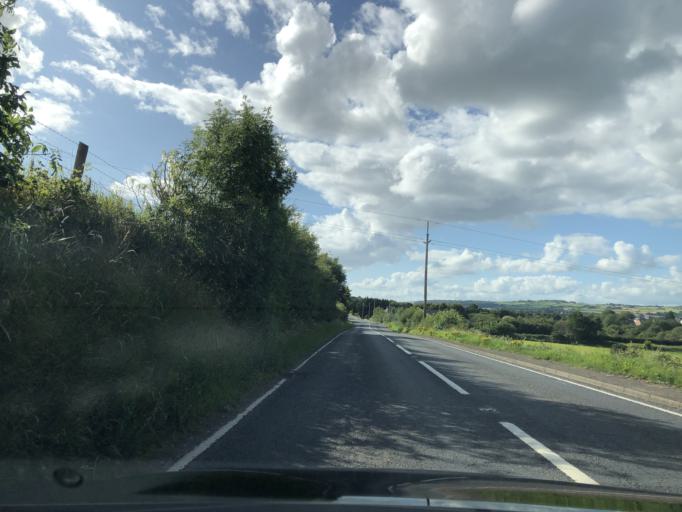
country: GB
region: Northern Ireland
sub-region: Castlereagh District
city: Dundonald
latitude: 54.5735
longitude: -5.7794
